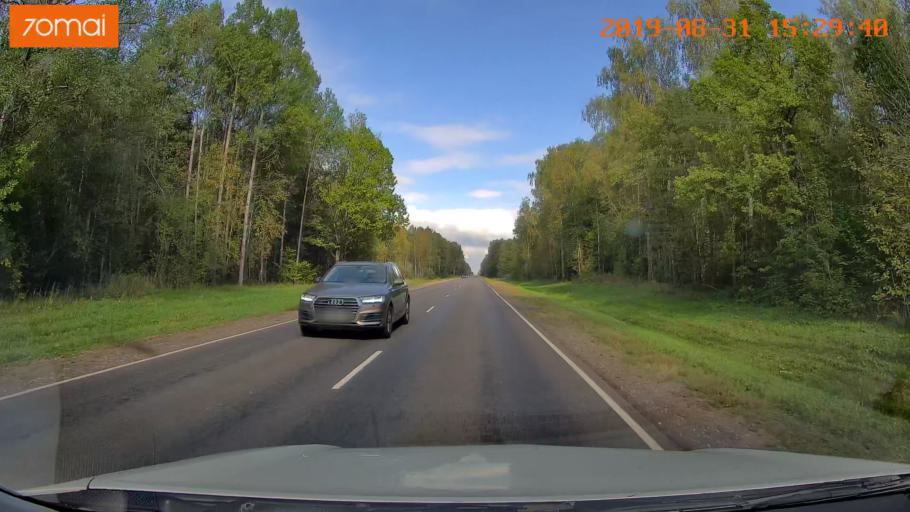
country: RU
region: Kaluga
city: Baryatino
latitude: 54.5705
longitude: 34.6113
